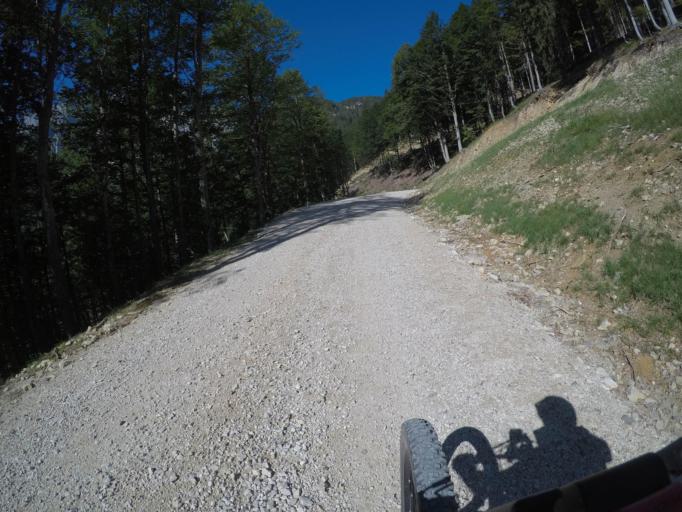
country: IT
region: Friuli Venezia Giulia
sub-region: Provincia di Udine
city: Malborghetto
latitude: 46.4567
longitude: 13.4592
